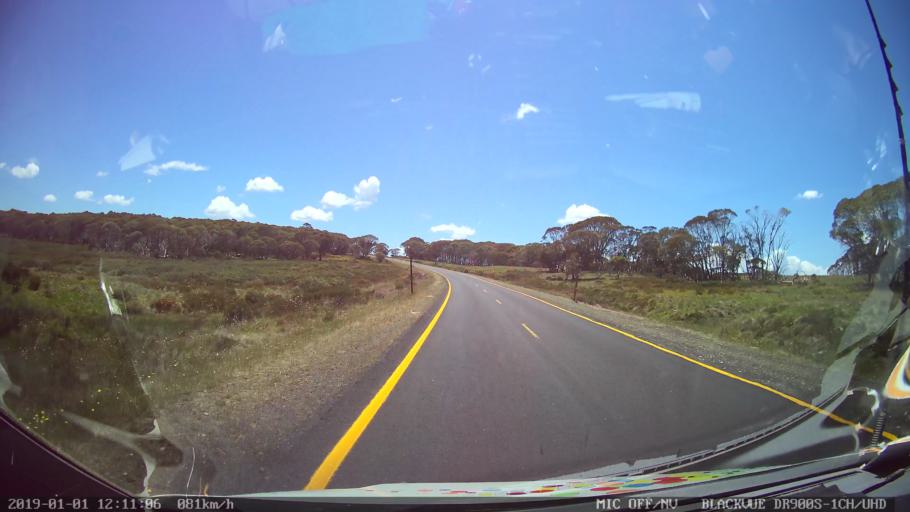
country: AU
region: New South Wales
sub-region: Tumut Shire
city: Tumut
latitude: -35.7877
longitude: 148.5058
